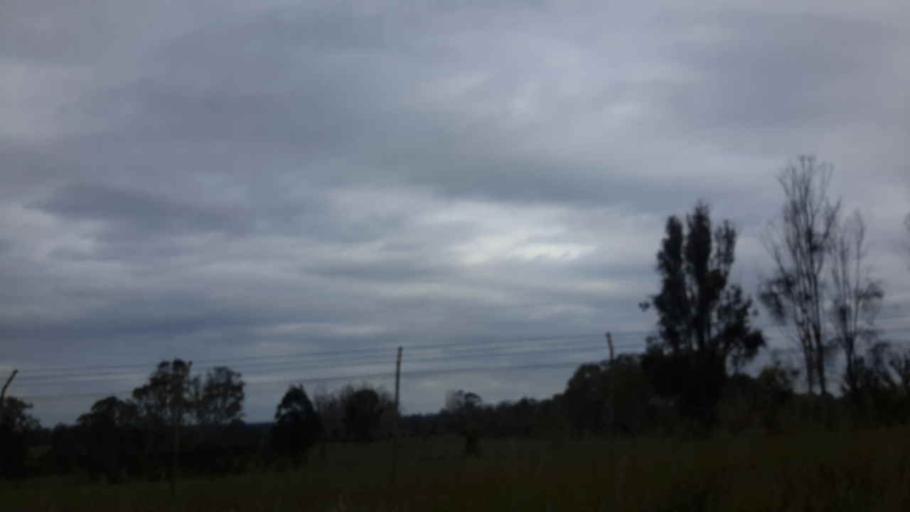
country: AU
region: New South Wales
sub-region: Penrith Municipality
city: Mulgoa
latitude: -33.8348
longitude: 150.6829
